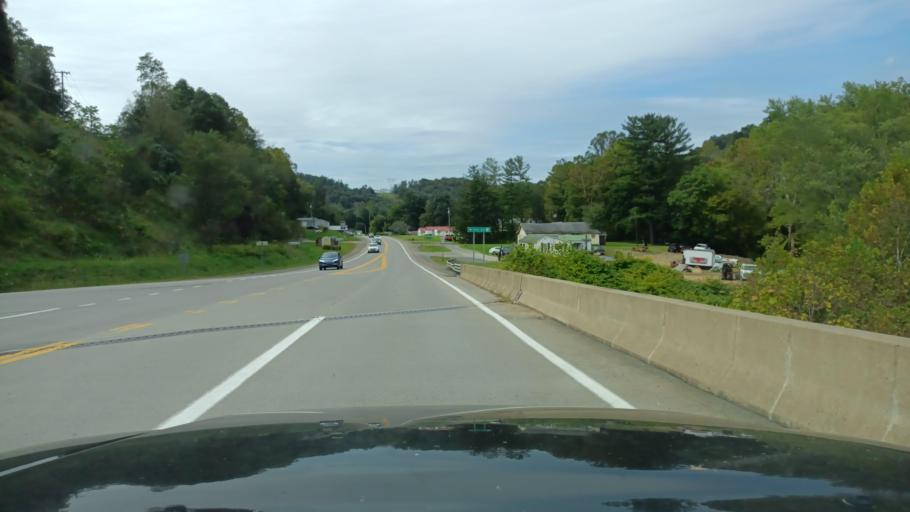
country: US
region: West Virginia
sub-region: Taylor County
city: Grafton
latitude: 39.3531
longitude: -80.0419
